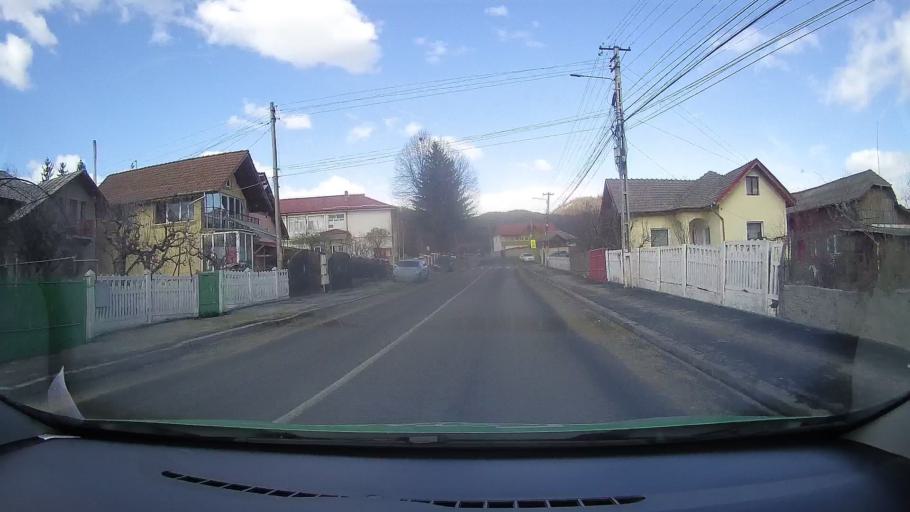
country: RO
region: Dambovita
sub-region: Comuna Fieni
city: Fieni
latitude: 45.1277
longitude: 25.4183
